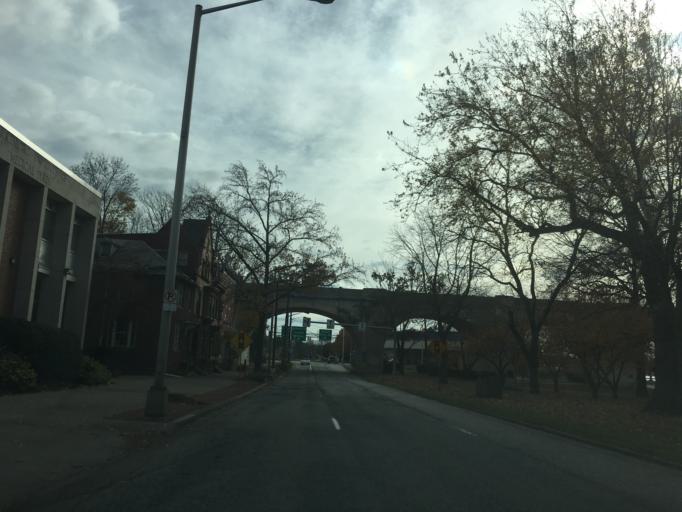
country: US
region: Pennsylvania
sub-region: Dauphin County
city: Harrisburg
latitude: 40.2562
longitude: -76.8784
